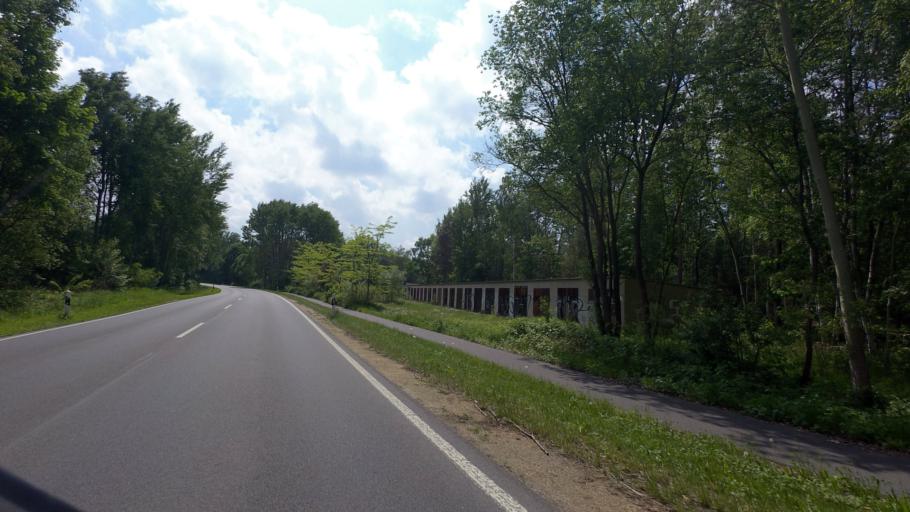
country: DE
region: Saxony
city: Weisswasser
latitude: 51.5216
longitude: 14.6062
